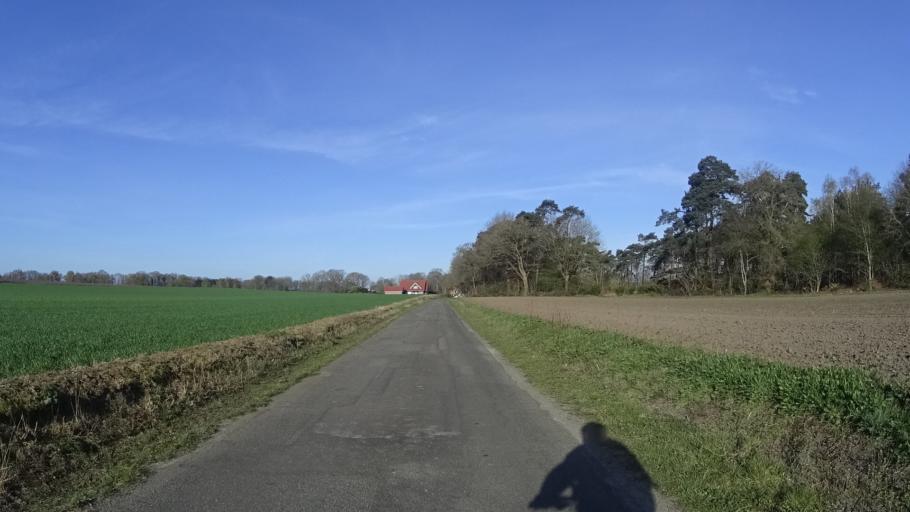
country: DE
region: Lower Saxony
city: Haren
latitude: 52.8131
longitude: 7.2638
